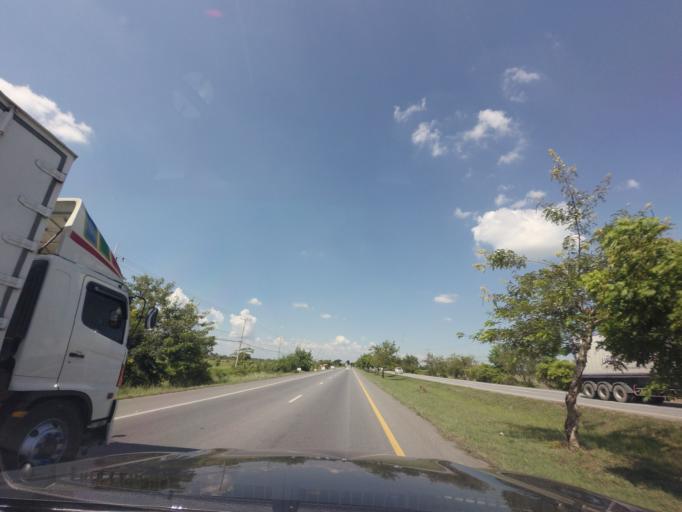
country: TH
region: Nakhon Ratchasima
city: Non Sung
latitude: 15.1313
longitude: 102.3076
